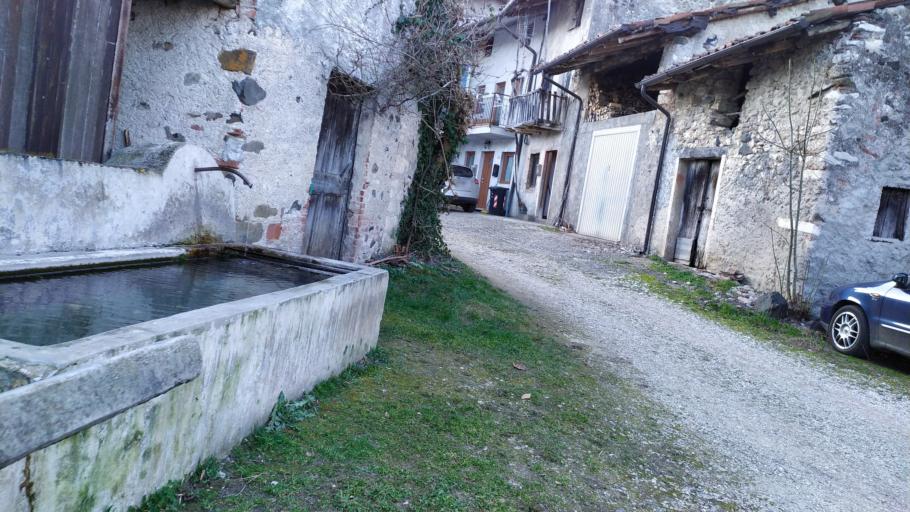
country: IT
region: Veneto
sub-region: Provincia di Vicenza
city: Monte di Malo
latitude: 45.6647
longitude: 11.3498
